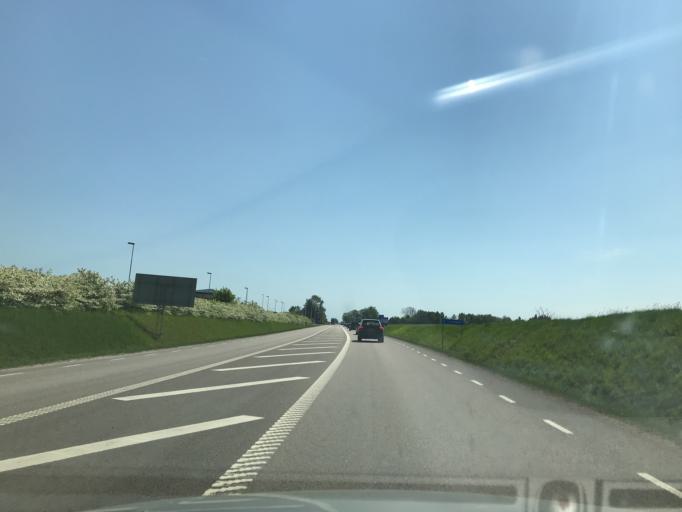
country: SE
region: Skane
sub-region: Astorps Kommun
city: Kvidinge
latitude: 56.1891
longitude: 13.0542
